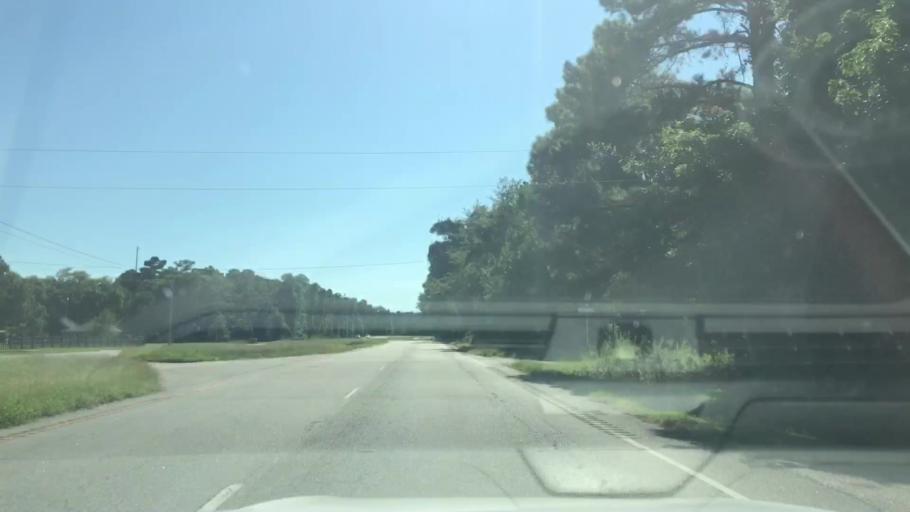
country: US
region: South Carolina
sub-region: Charleston County
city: Awendaw
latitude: 33.0494
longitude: -79.5604
